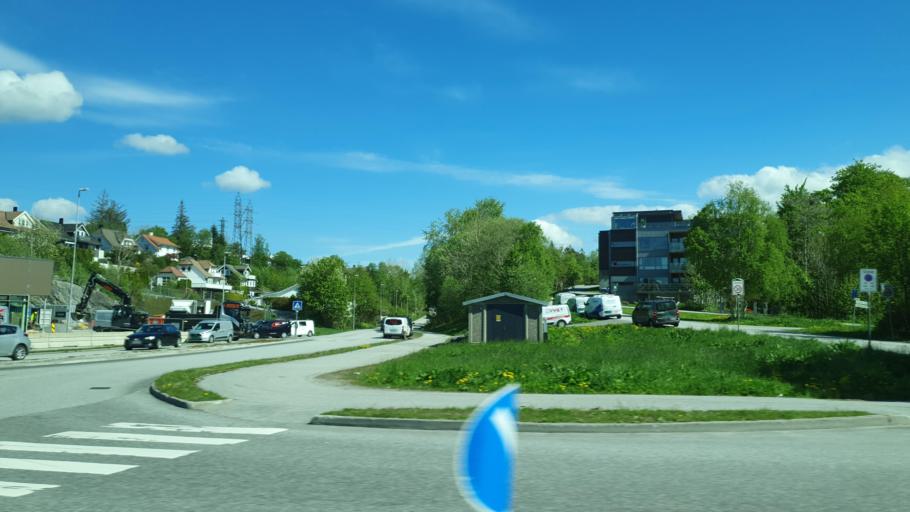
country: NO
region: More og Romsdal
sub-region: Sula
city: Langevag
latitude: 62.4719
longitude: 6.2399
